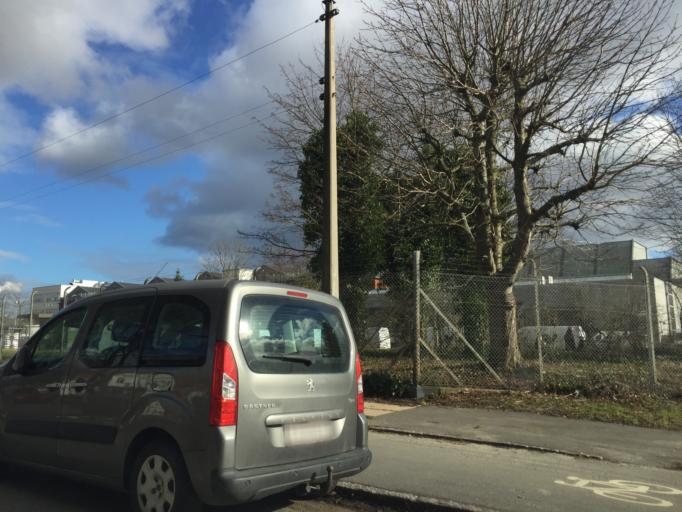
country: DK
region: Capital Region
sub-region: Frederiksberg Kommune
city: Frederiksberg
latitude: 55.6467
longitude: 12.5351
